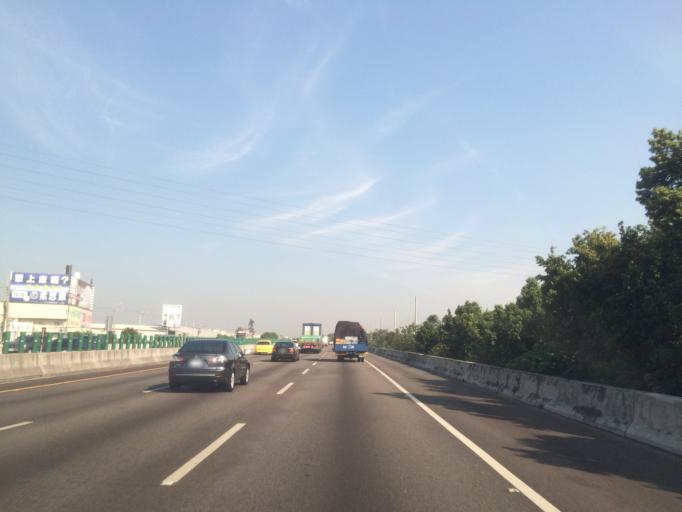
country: TW
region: Taiwan
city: Fengyuan
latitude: 24.2290
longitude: 120.6857
